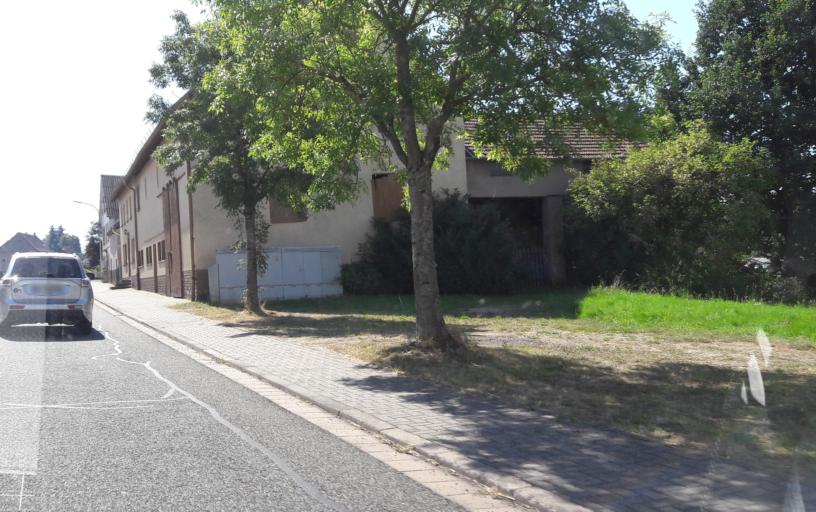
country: DE
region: Rheinland-Pfalz
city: Gimbweiler
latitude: 49.5683
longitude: 7.1737
